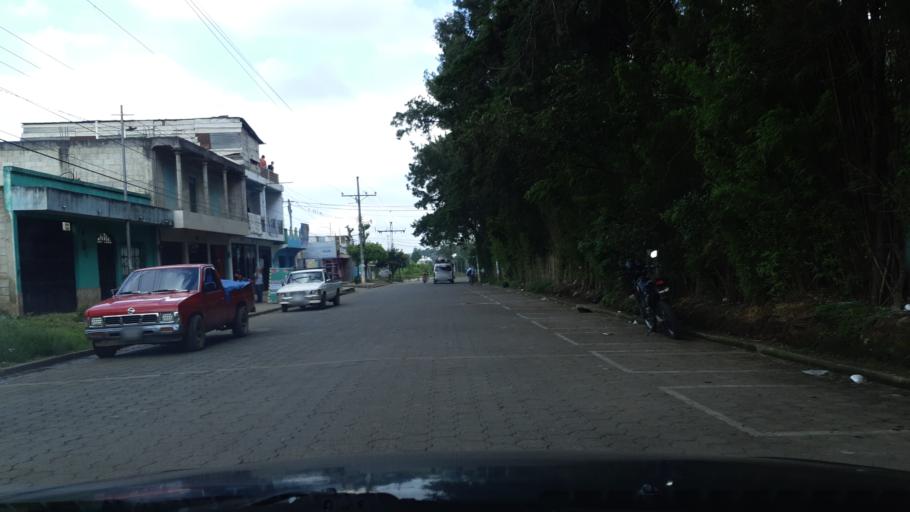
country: GT
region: Chimaltenango
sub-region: Municipio de Chimaltenango
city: Chimaltenango
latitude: 14.6691
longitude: -90.8108
